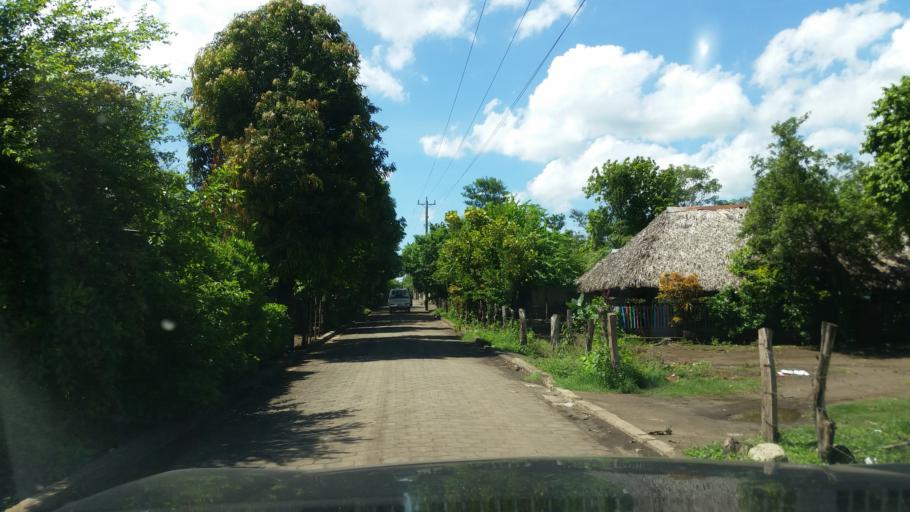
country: NI
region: Chinandega
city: Puerto Morazan
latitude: 12.7672
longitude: -87.1357
